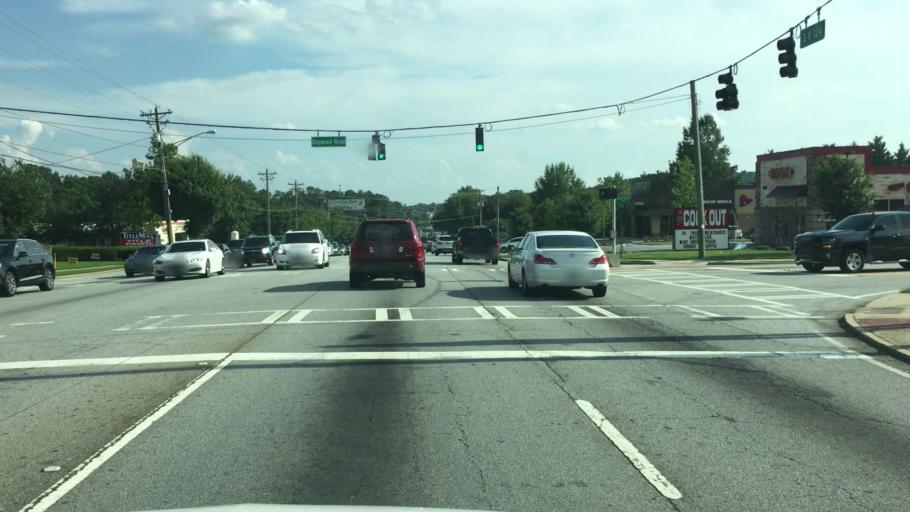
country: US
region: Georgia
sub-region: Gwinnett County
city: Snellville
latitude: 33.8697
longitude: -84.0153
